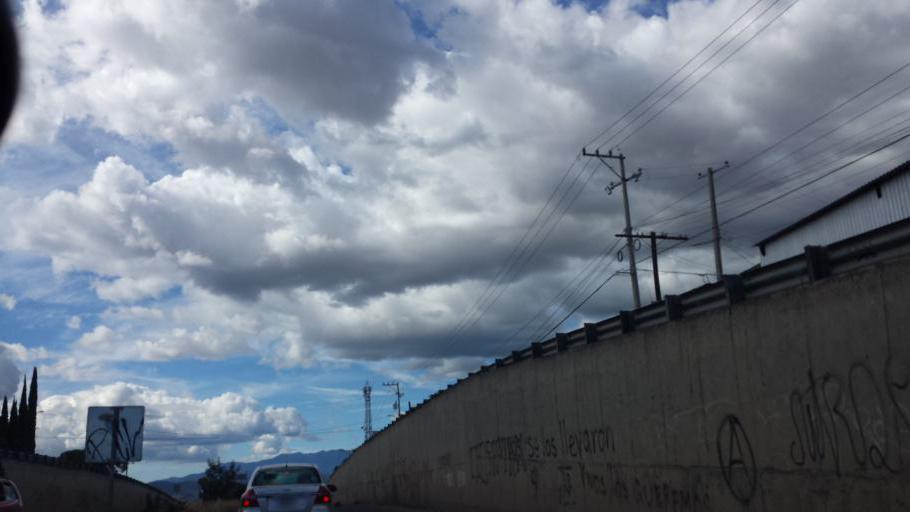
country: MX
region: Oaxaca
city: Tlacolula de Matamoros
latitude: 16.9580
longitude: -96.4735
